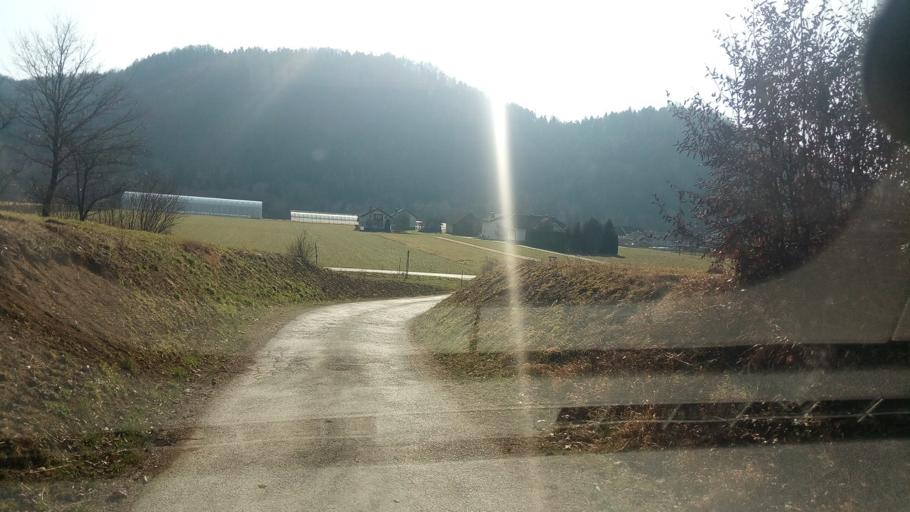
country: SI
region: Vodice
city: Vodice
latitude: 46.1509
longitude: 14.4879
